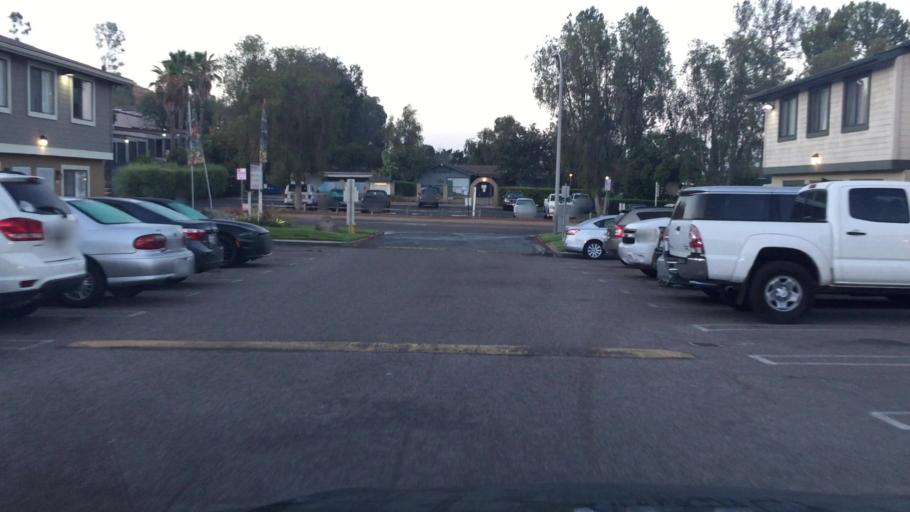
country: US
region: California
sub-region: San Diego County
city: Bostonia
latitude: 32.8196
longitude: -116.9556
